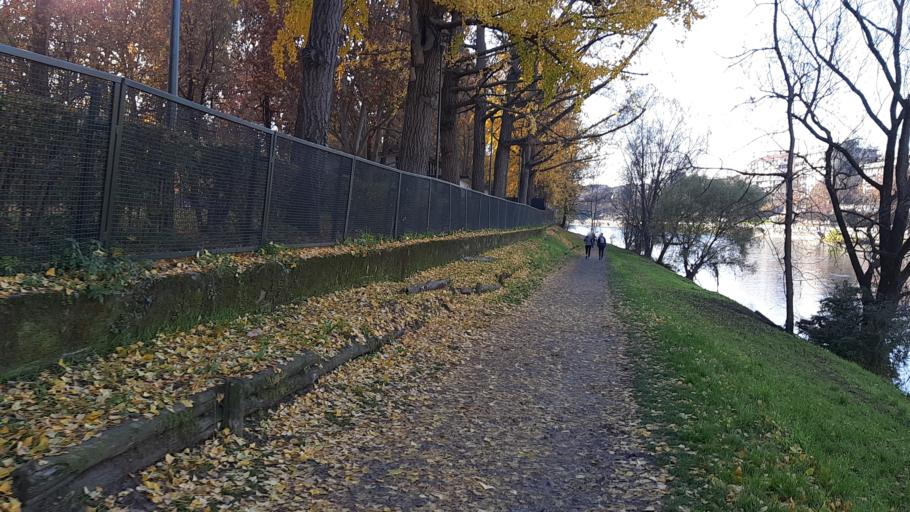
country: IT
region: Piedmont
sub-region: Provincia di Torino
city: Turin
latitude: 45.0674
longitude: 7.7073
